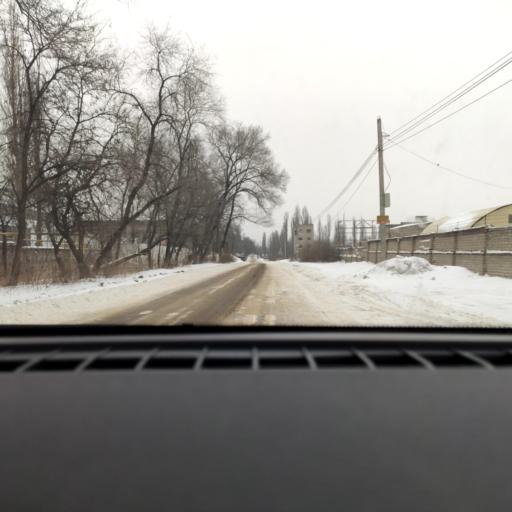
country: RU
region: Voronezj
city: Voronezh
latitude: 51.6465
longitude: 39.2867
